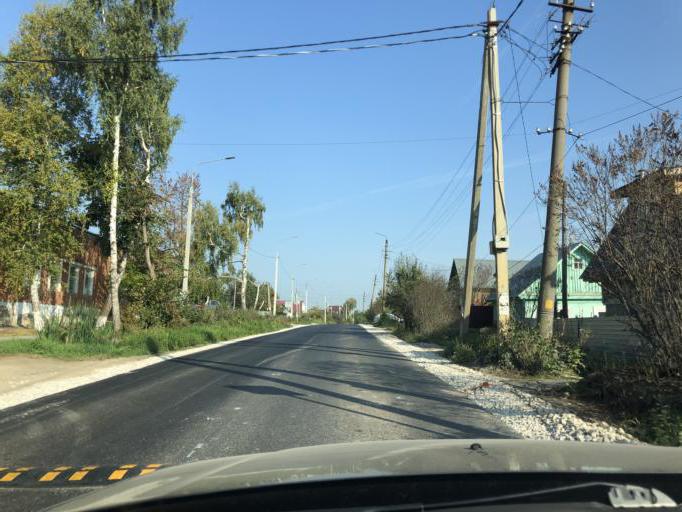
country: RU
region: Tula
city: Leninskiy
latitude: 54.2884
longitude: 37.4657
